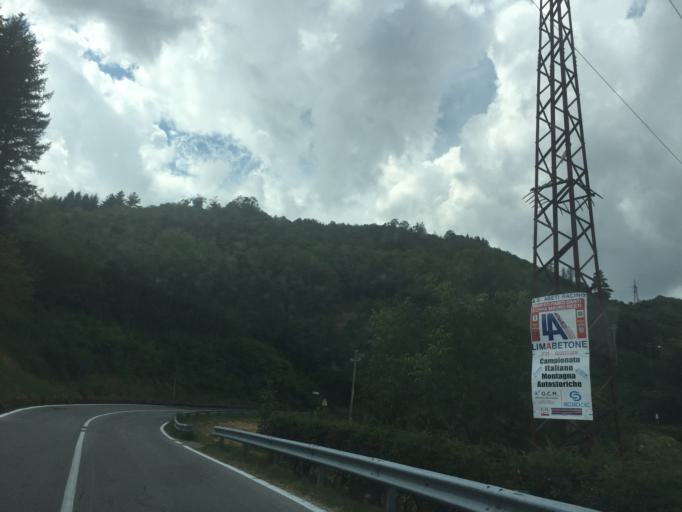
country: IT
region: Tuscany
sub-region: Provincia di Pistoia
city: Cutigliano
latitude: 44.1036
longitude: 10.7439
